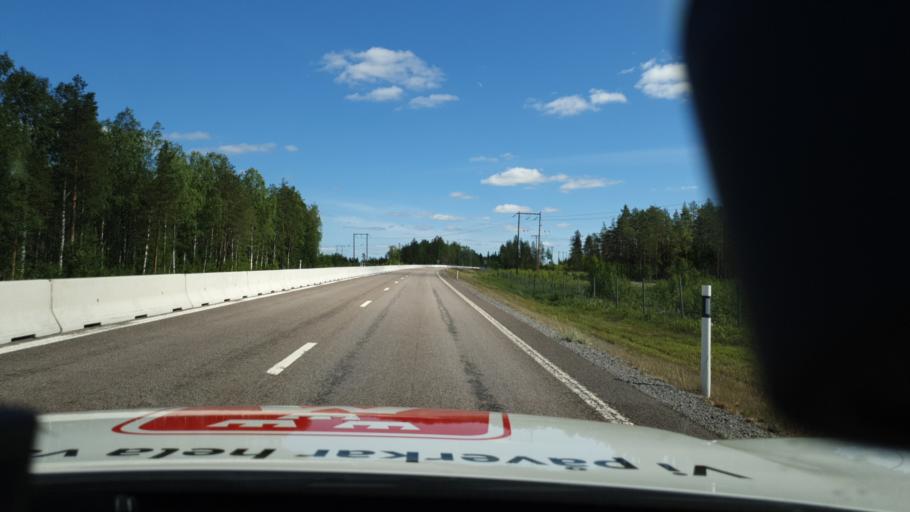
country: SE
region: Norrbotten
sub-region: Kalix Kommun
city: Toere
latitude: 65.9101
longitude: 22.8209
